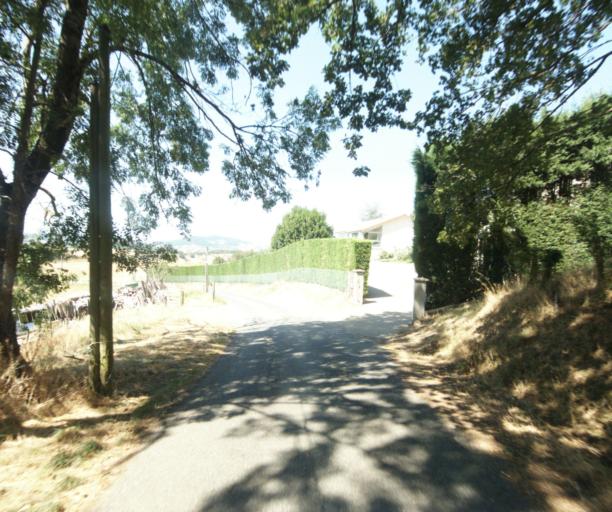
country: FR
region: Rhone-Alpes
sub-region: Departement du Rhone
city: Sainte-Foy-l'Argentiere
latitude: 45.7199
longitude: 4.5215
